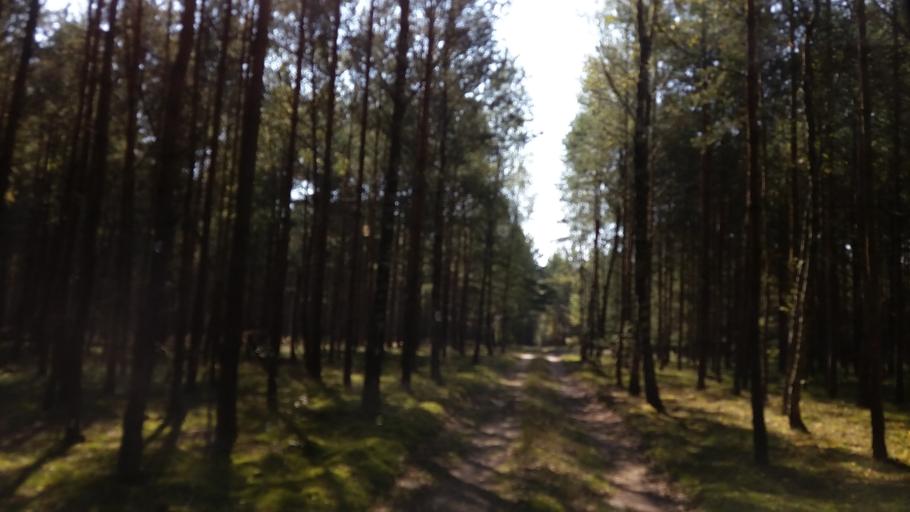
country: PL
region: West Pomeranian Voivodeship
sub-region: Powiat walecki
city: Tuczno
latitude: 53.2150
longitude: 16.0210
